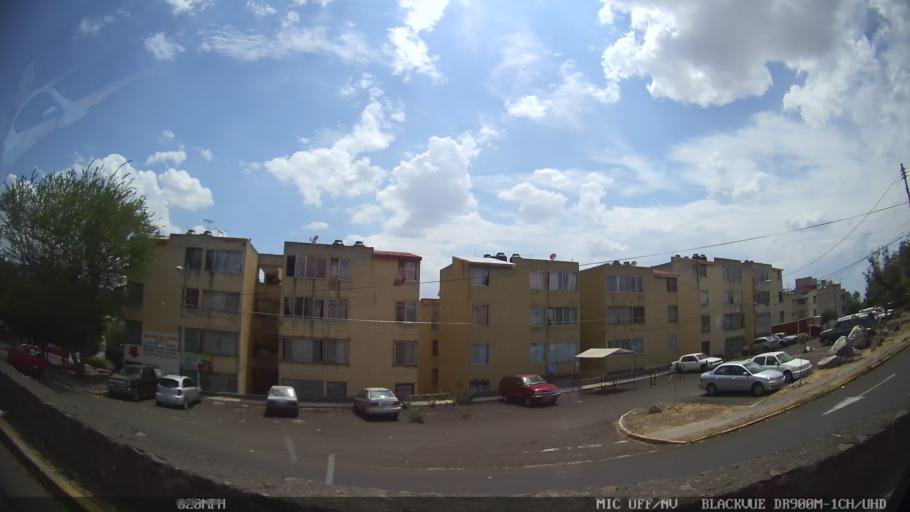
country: MX
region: Jalisco
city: Tonala
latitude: 20.6241
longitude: -103.2515
